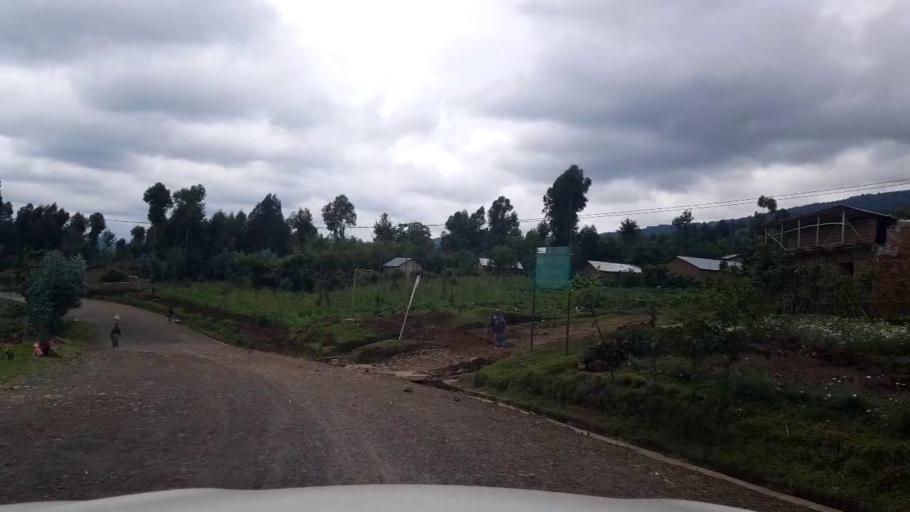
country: RW
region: Northern Province
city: Musanze
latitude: -1.5421
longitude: 29.5311
